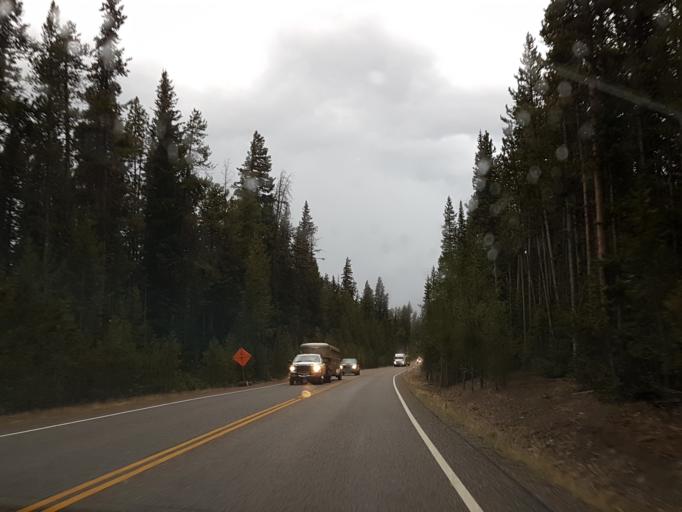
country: US
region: Montana
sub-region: Gallatin County
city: West Yellowstone
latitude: 44.4644
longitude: -110.5153
